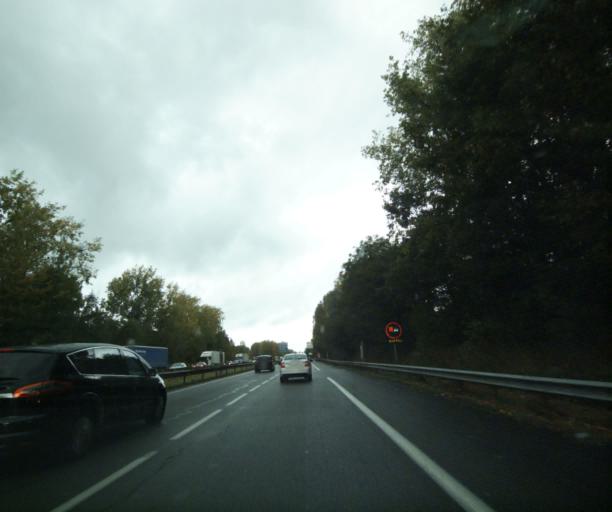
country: FR
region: Nord-Pas-de-Calais
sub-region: Departement du Nord
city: Mouvaux
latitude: 50.7133
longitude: 3.1237
